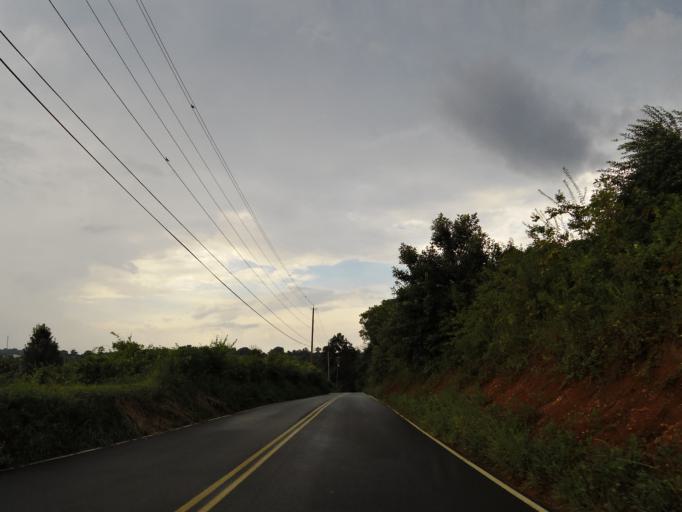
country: US
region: Tennessee
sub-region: Sevier County
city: Seymour
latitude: 35.8591
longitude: -83.7483
